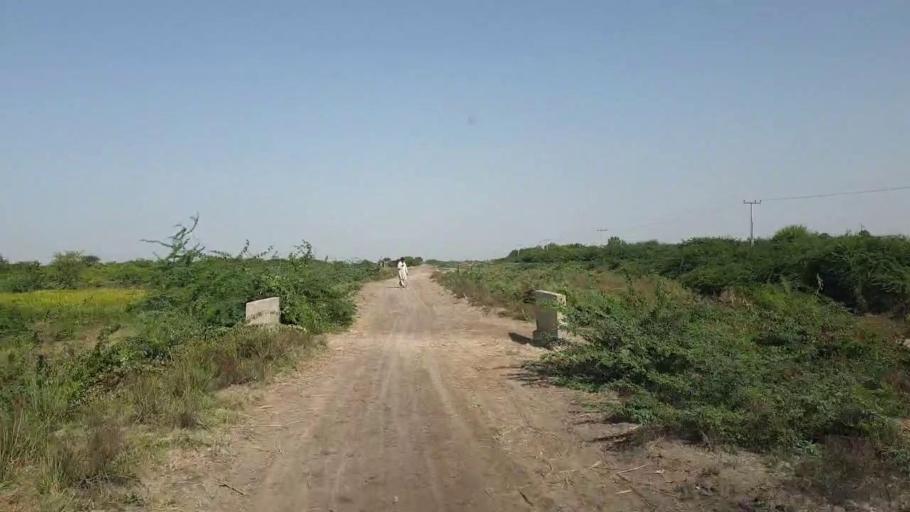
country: PK
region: Sindh
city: Tando Bago
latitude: 24.6977
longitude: 69.0703
